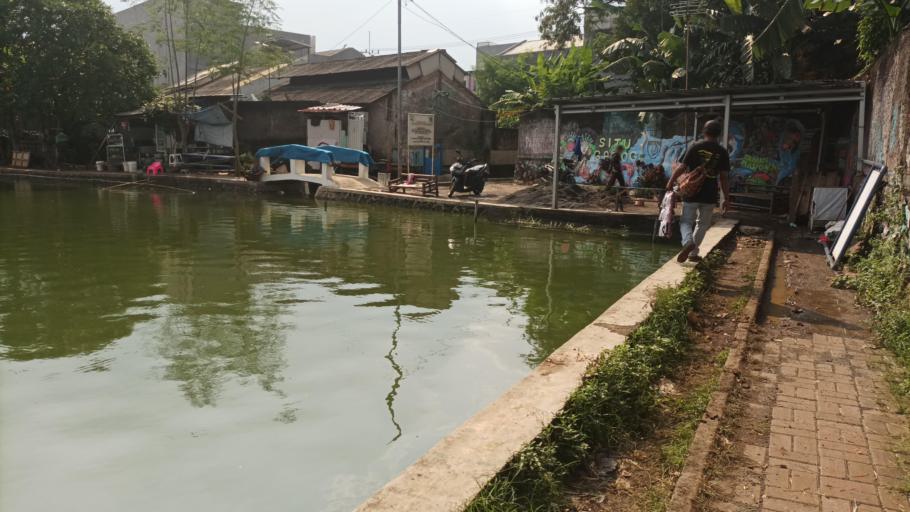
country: ID
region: West Java
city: Depok
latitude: -6.3729
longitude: 106.8685
